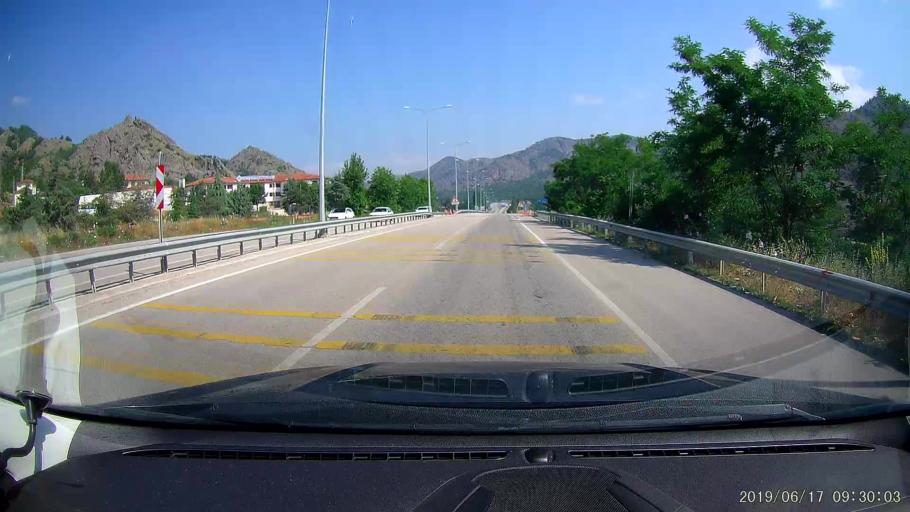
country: TR
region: Amasya
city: Amasya
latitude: 40.7016
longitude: 35.8058
